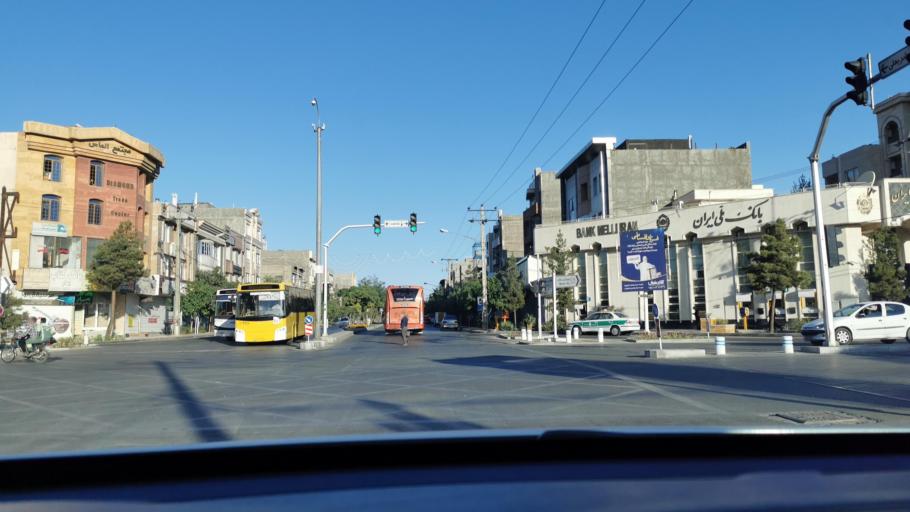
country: IR
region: Razavi Khorasan
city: Mashhad
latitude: 36.3521
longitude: 59.5018
